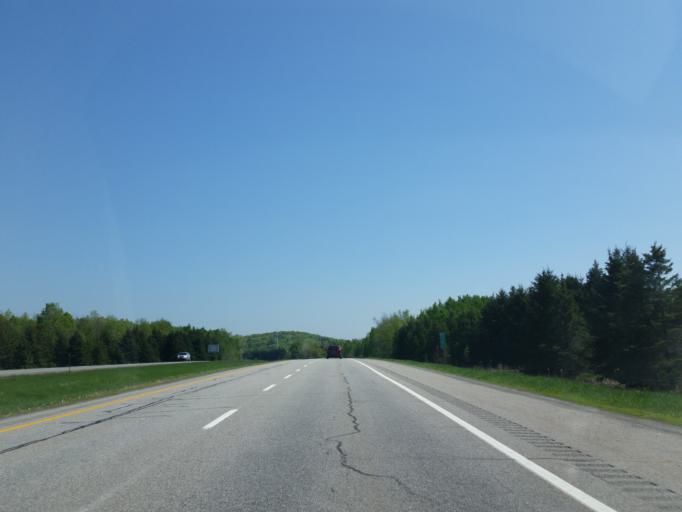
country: CA
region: Quebec
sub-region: Outaouais
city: Gatineau
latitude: 45.4906
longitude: -75.7984
